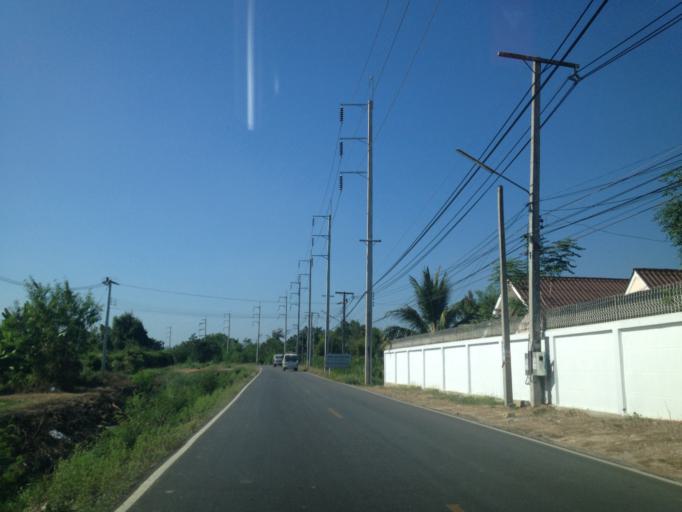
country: TH
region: Chiang Mai
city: Hang Dong
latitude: 18.6738
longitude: 98.9127
